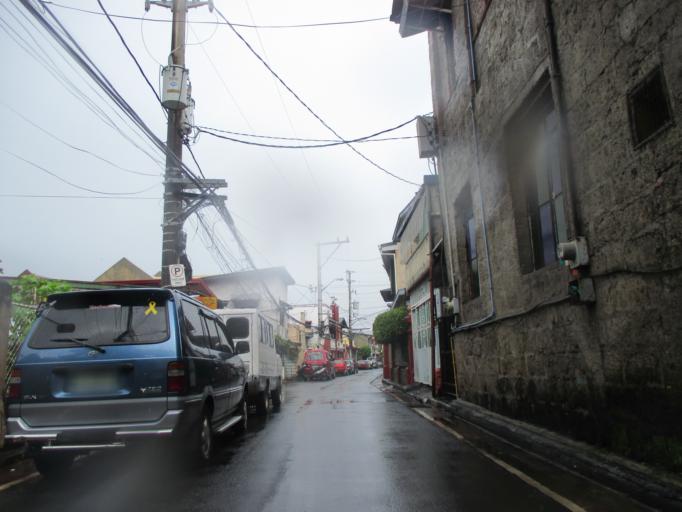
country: PH
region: Metro Manila
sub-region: Marikina
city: Calumpang
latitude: 14.6304
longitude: 121.0956
